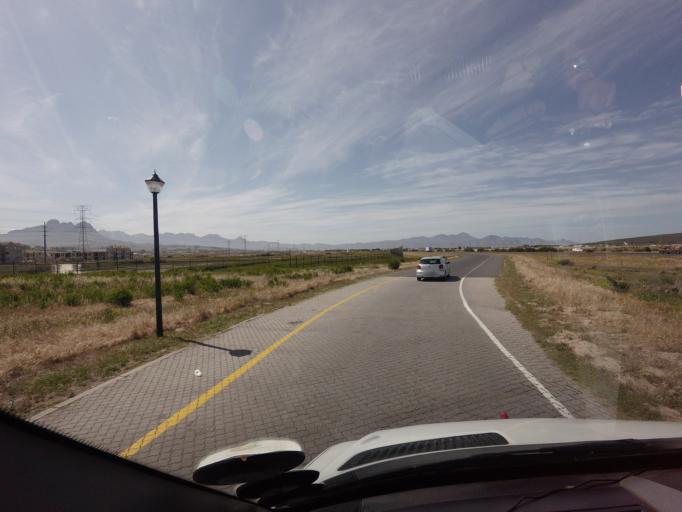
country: ZA
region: Western Cape
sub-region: Cape Winelands District Municipality
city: Stellenbosch
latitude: -34.0481
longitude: 18.7579
